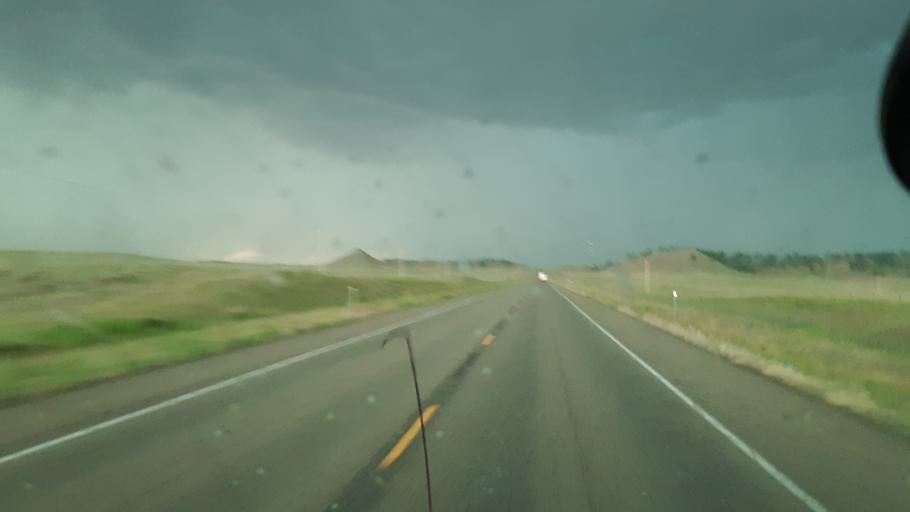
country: US
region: Montana
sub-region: Powder River County
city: Broadus
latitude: 45.4696
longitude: -105.4788
